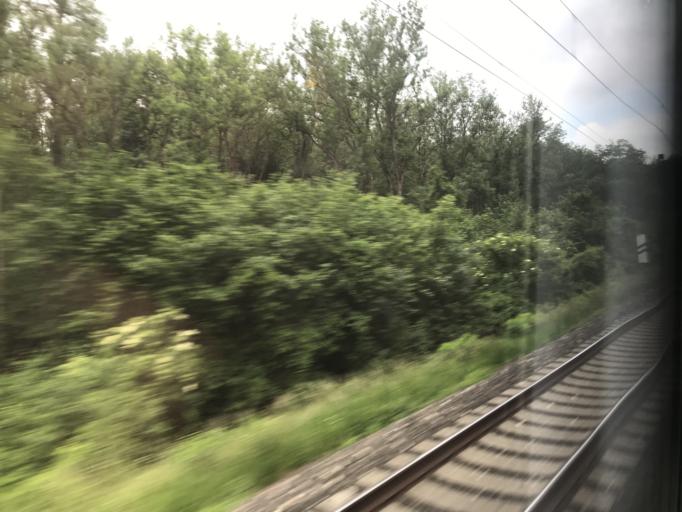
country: DE
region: Bavaria
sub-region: Swabia
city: Leipheim
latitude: 48.4403
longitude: 10.1913
